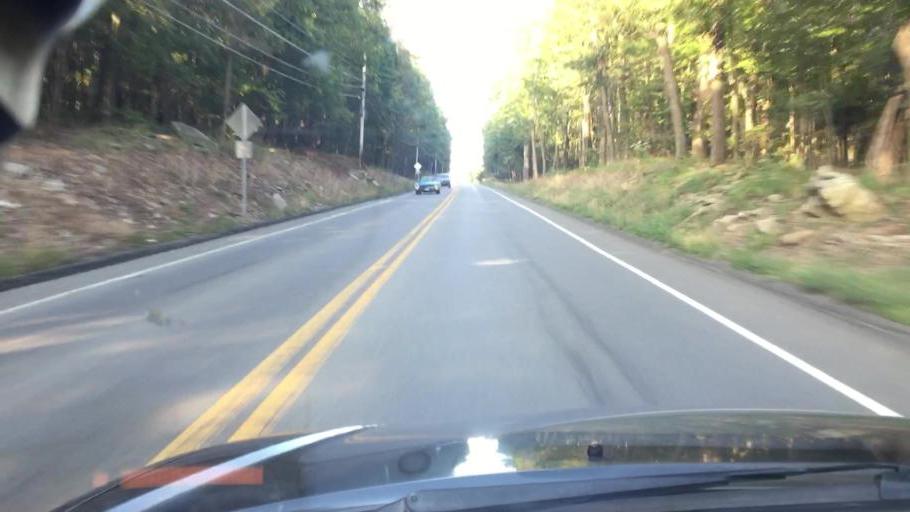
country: US
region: Pennsylvania
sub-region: Carbon County
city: Jim Thorpe
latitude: 40.8904
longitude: -75.6970
